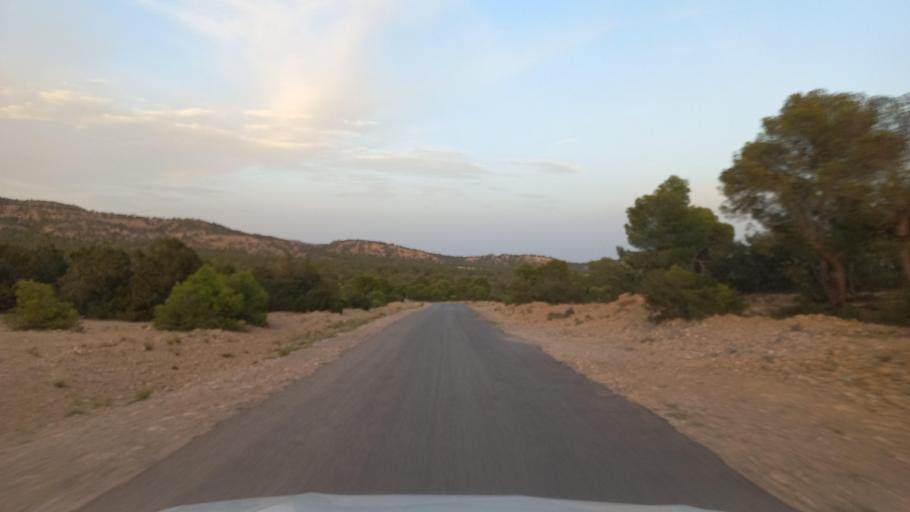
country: TN
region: Al Qasrayn
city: Sbiba
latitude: 35.4123
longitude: 8.9390
